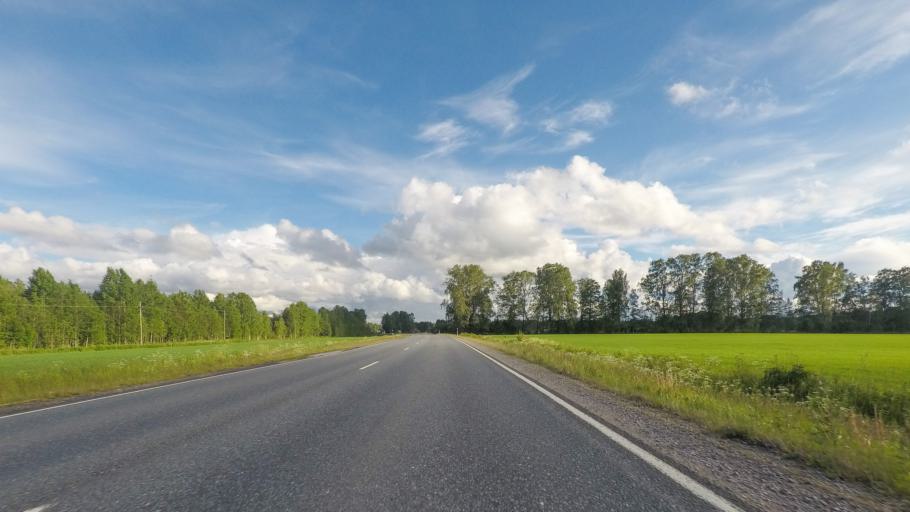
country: FI
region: Paijanne Tavastia
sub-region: Lahti
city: Hartola
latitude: 61.6140
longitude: 26.0073
